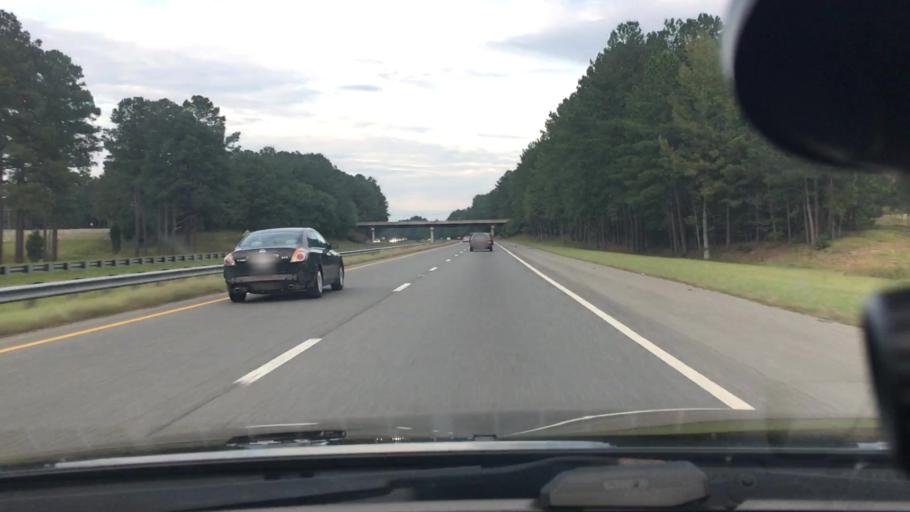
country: US
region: North Carolina
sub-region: Chatham County
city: Farmville
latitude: 35.5858
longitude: -79.1244
